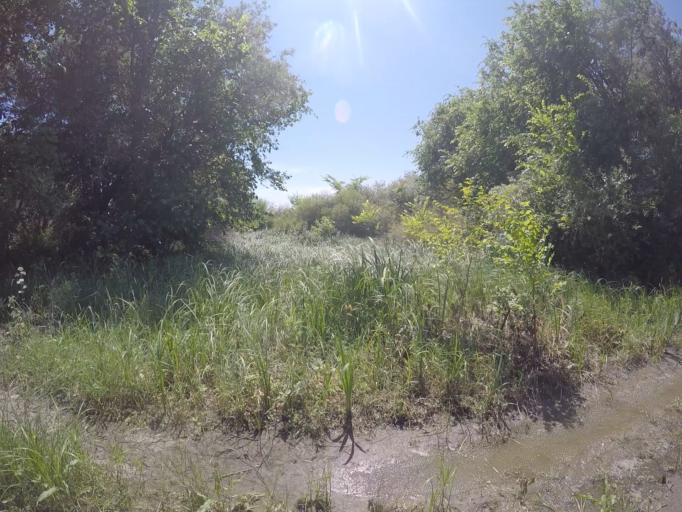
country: RU
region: Saratov
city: Krasnoarmeysk
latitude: 51.1526
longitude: 45.9042
